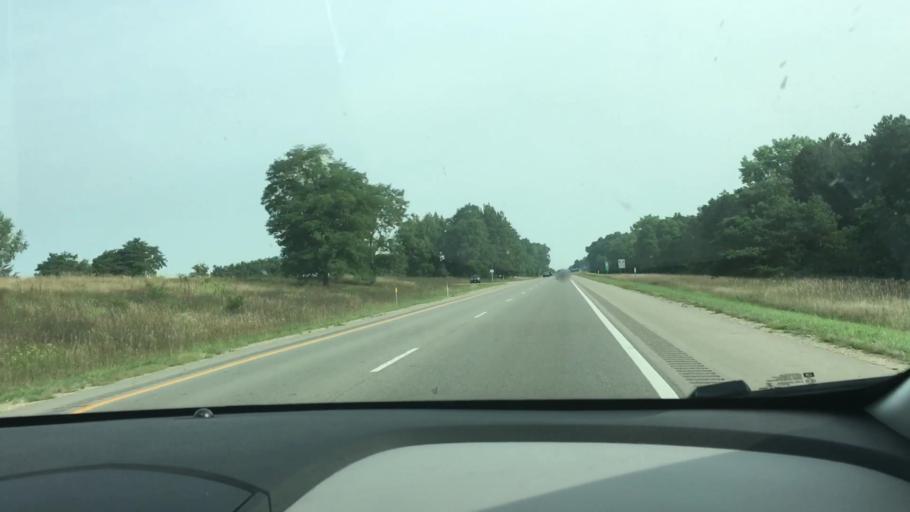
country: US
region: Michigan
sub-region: Kalamazoo County
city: Schoolcraft
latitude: 42.1638
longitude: -85.6443
